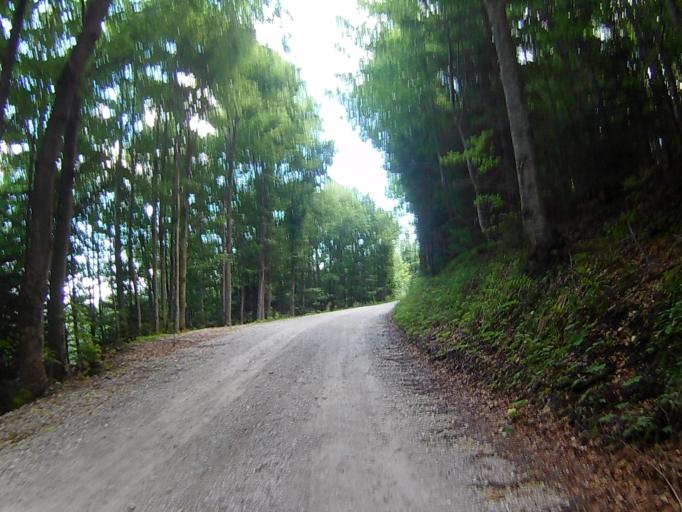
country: SI
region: Ruse
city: Ruse
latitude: 46.4998
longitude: 15.4865
